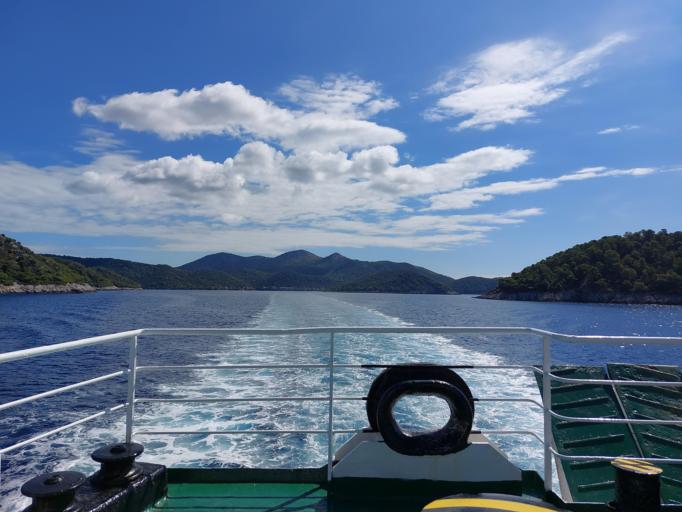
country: HR
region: Dubrovacko-Neretvanska
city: Smokvica
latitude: 42.7517
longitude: 16.7915
